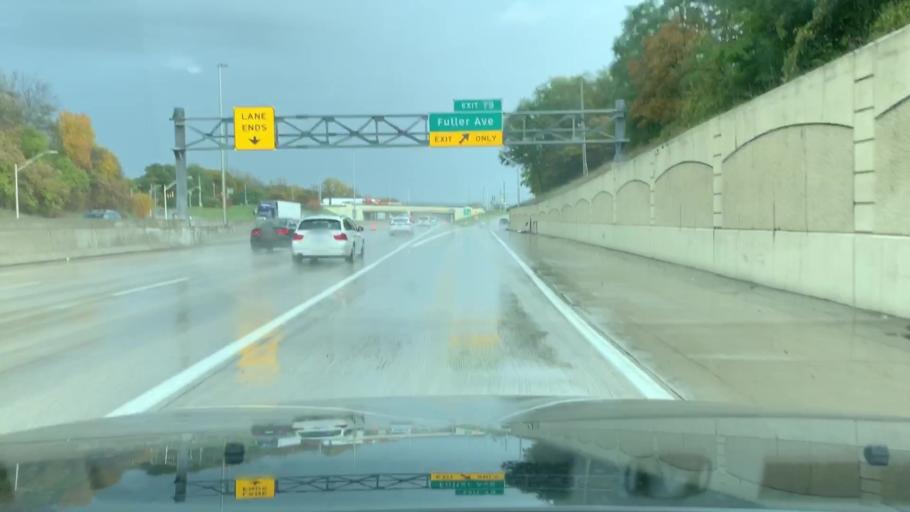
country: US
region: Michigan
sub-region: Kent County
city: Grand Rapids
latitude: 42.9733
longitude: -85.6438
